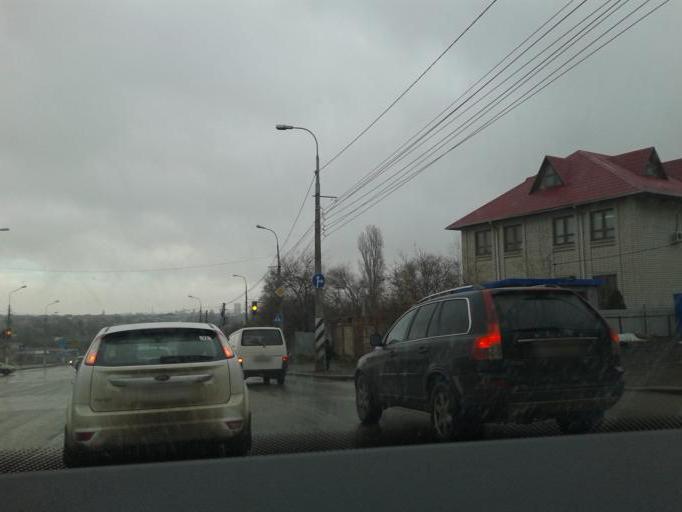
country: RU
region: Volgograd
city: Volgograd
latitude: 48.6833
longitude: 44.4493
